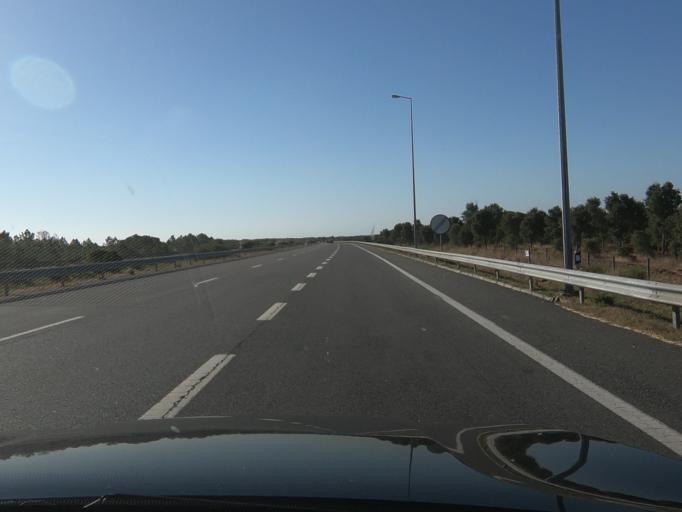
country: PT
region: Setubal
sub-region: Grandola
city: Grandola
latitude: 38.1654
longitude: -8.4897
